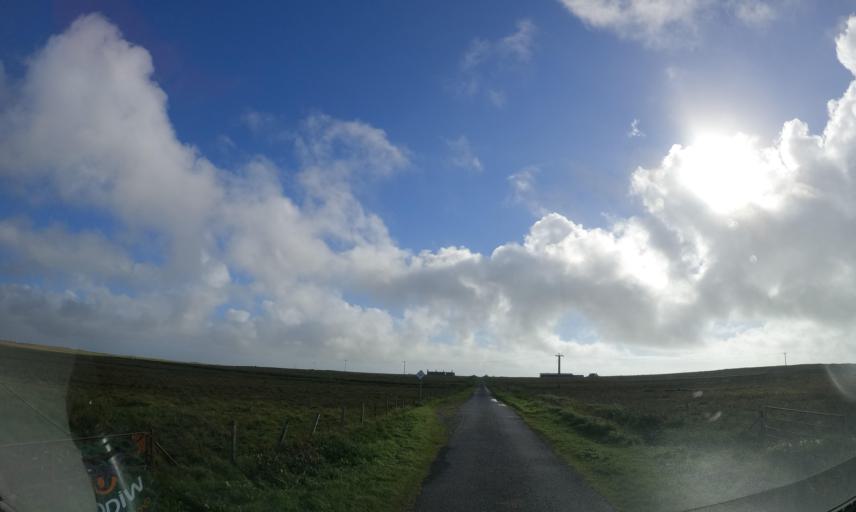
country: GB
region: Scotland
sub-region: Eilean Siar
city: Barra
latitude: 56.4835
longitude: -6.9244
